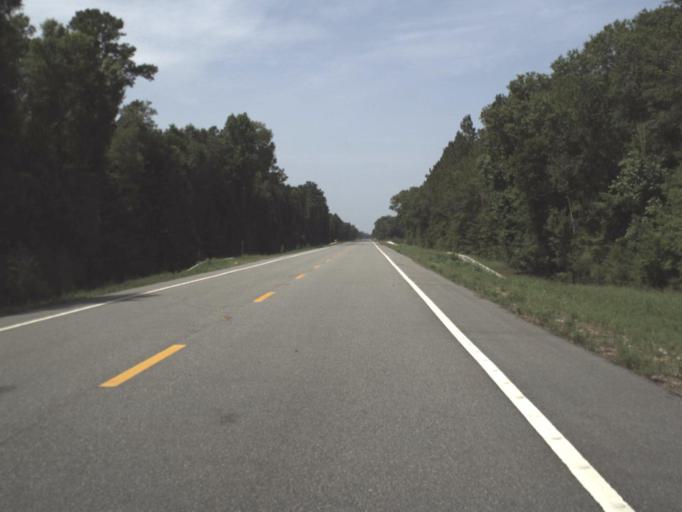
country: US
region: Florida
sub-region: Taylor County
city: Steinhatchee
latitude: 29.8190
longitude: -83.3162
